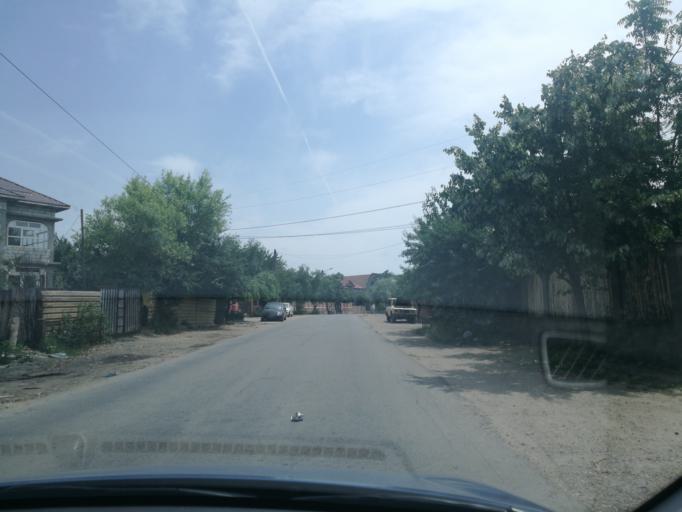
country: RO
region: Ilfov
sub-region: Comuna Jilava
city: Jilava
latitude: 44.3212
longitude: 26.0992
